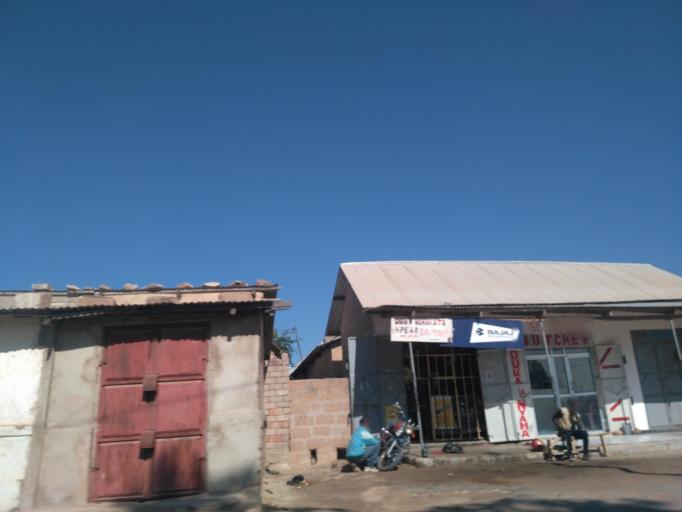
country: TZ
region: Dodoma
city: Dodoma
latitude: -6.1415
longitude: 35.7466
